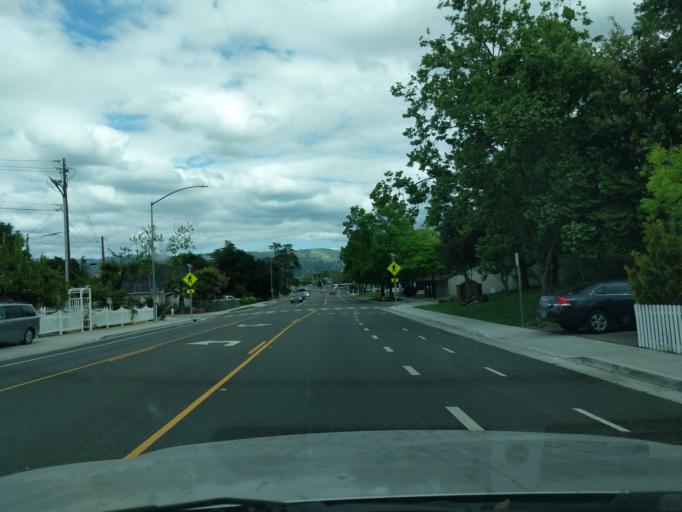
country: US
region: California
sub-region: Santa Clara County
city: Morgan Hill
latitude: 37.1243
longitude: -121.6529
